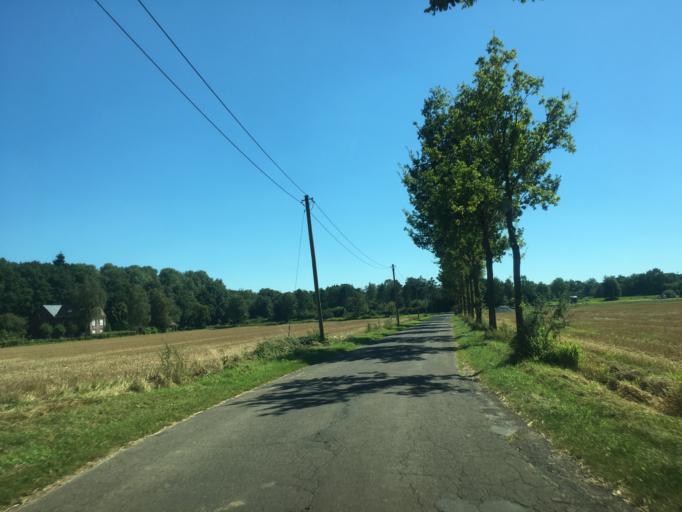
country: DE
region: North Rhine-Westphalia
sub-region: Regierungsbezirk Munster
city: Muenster
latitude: 51.9949
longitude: 7.5735
